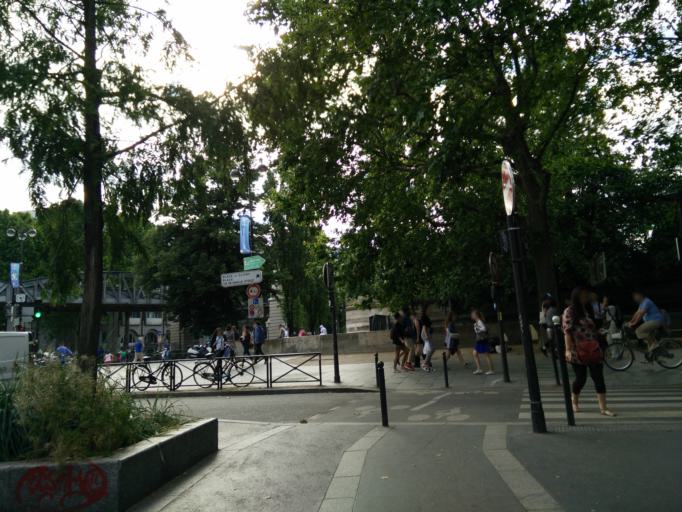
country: FR
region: Ile-de-France
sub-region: Departement de Seine-Saint-Denis
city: Le Pre-Saint-Gervais
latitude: 48.8831
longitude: 2.3709
